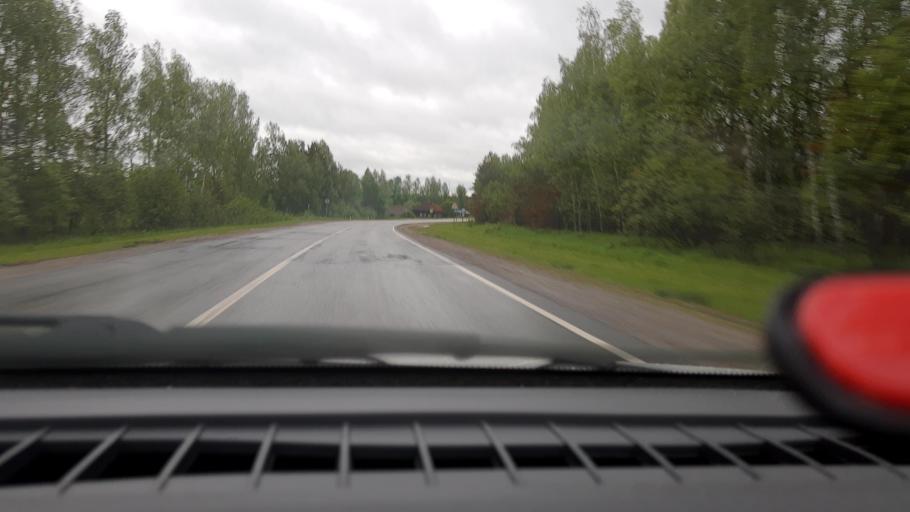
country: RU
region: Nizjnij Novgorod
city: Krasnyye Baki
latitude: 57.0095
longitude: 45.1122
